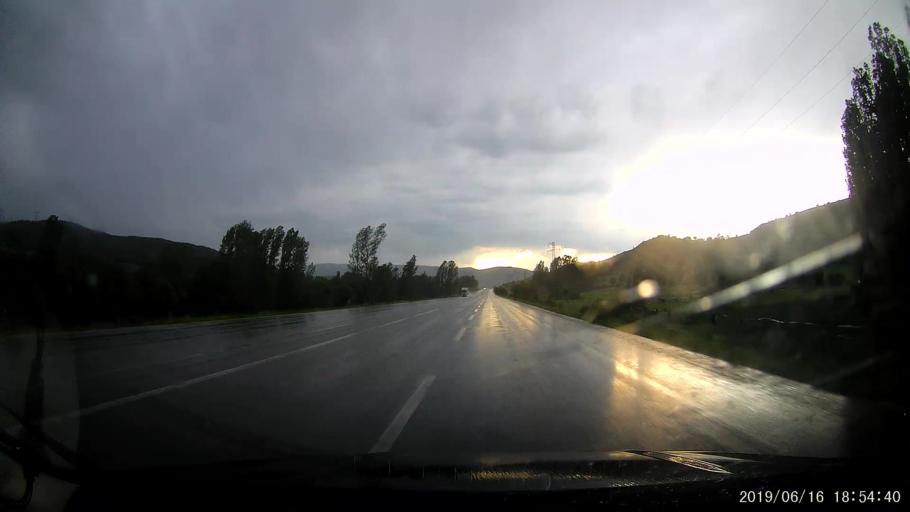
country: TR
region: Erzincan
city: Catalcam
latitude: 39.8977
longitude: 38.8479
